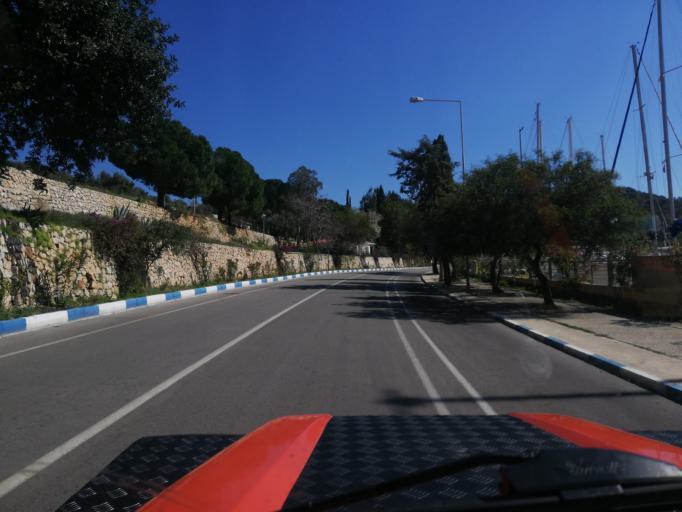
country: TR
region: Antalya
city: Kas
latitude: 36.2049
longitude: 29.6332
